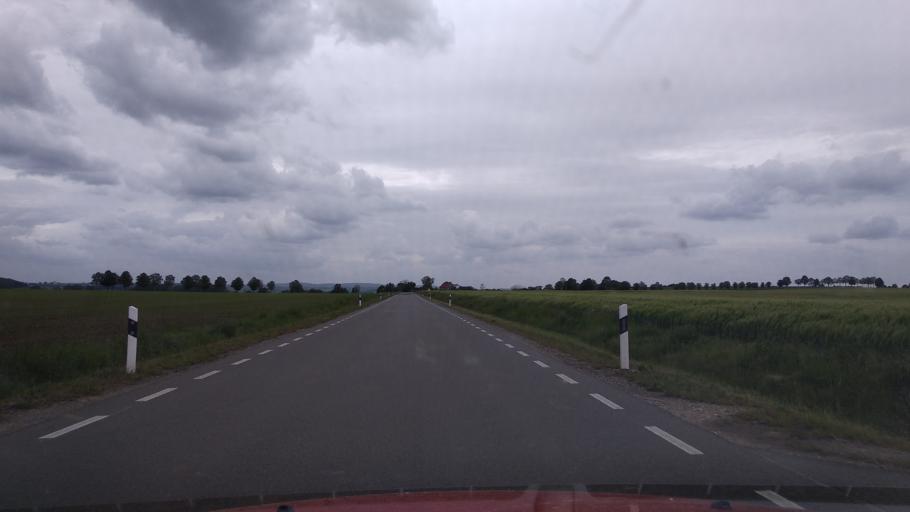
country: DE
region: North Rhine-Westphalia
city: Borgentreich
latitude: 51.5388
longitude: 9.2544
